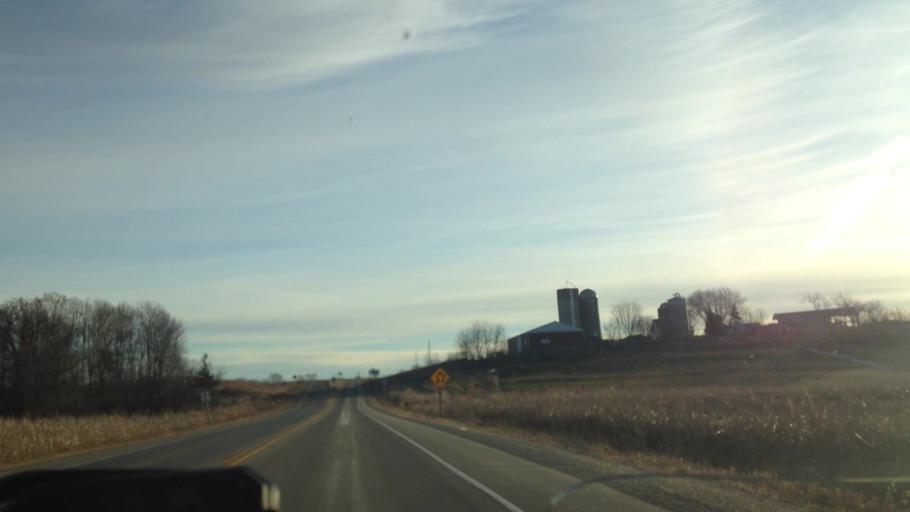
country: US
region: Wisconsin
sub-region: Dodge County
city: Theresa
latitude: 43.5369
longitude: -88.4105
